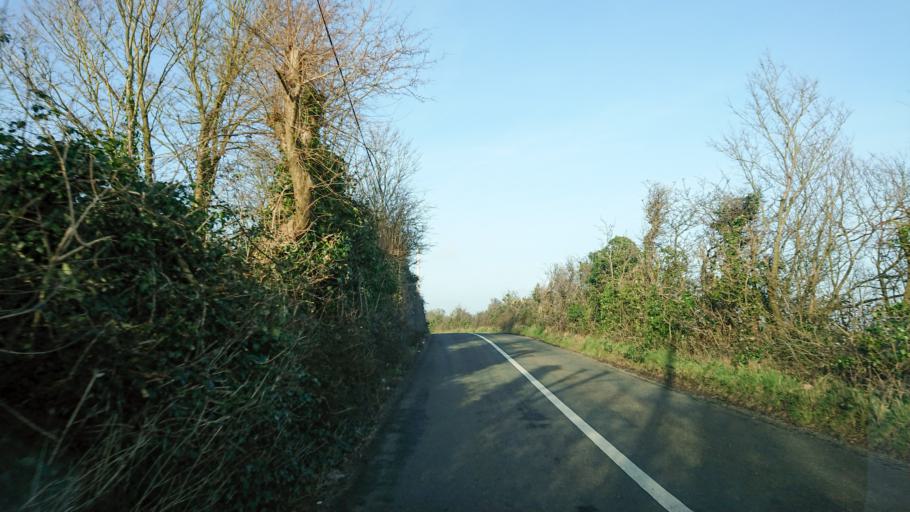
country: IE
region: Munster
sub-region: Waterford
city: Tra Mhor
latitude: 52.1766
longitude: -7.1183
